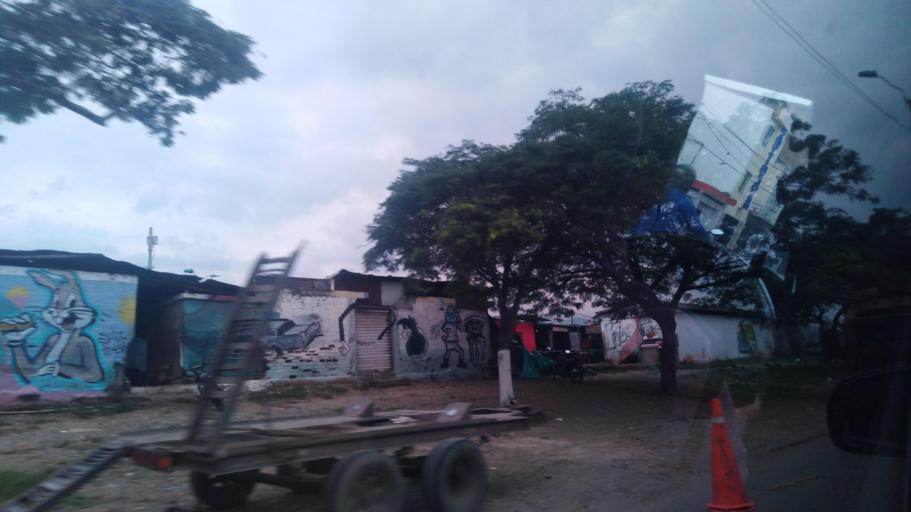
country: CO
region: Valle del Cauca
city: Cali
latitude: 3.4263
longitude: -76.5202
